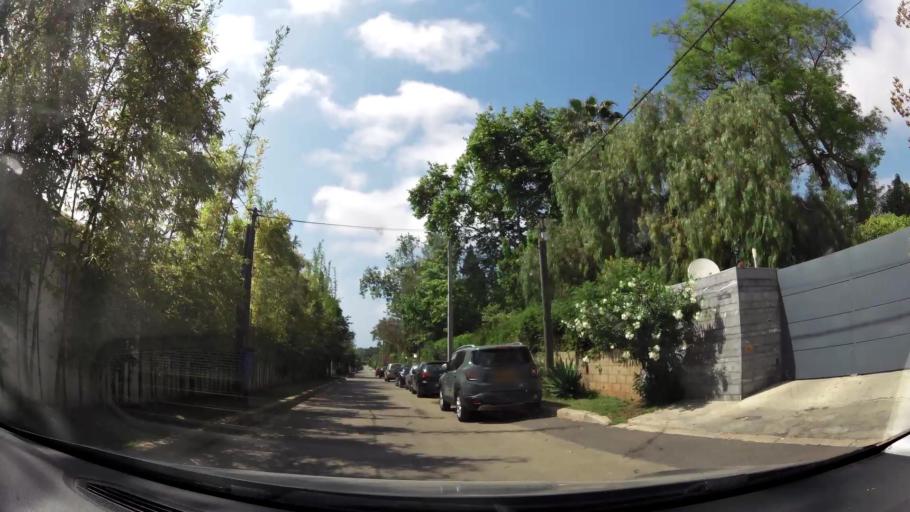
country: MA
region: Rabat-Sale-Zemmour-Zaer
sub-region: Rabat
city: Rabat
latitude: 33.9813
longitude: -6.8334
